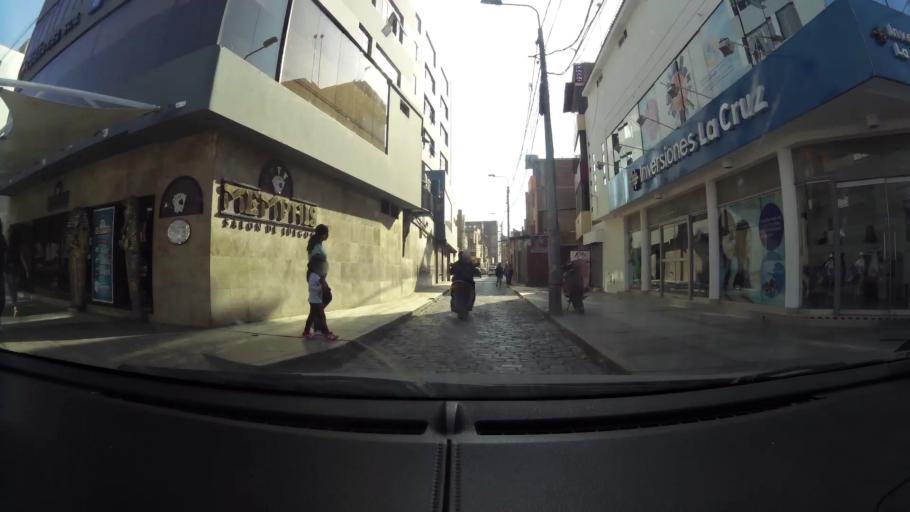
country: PE
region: Lambayeque
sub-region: Provincia de Chiclayo
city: Chiclayo
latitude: -6.7742
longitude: -79.8388
